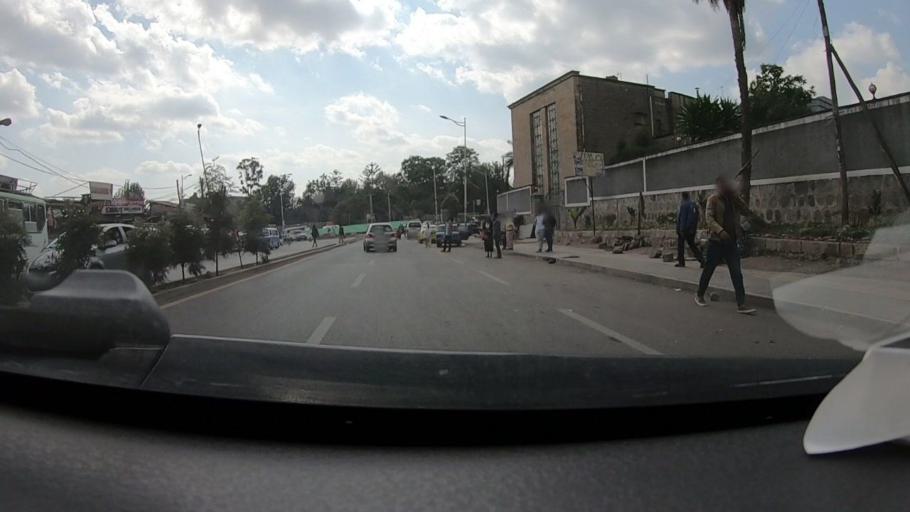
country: ET
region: Adis Abeba
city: Addis Ababa
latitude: 9.0440
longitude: 38.7634
